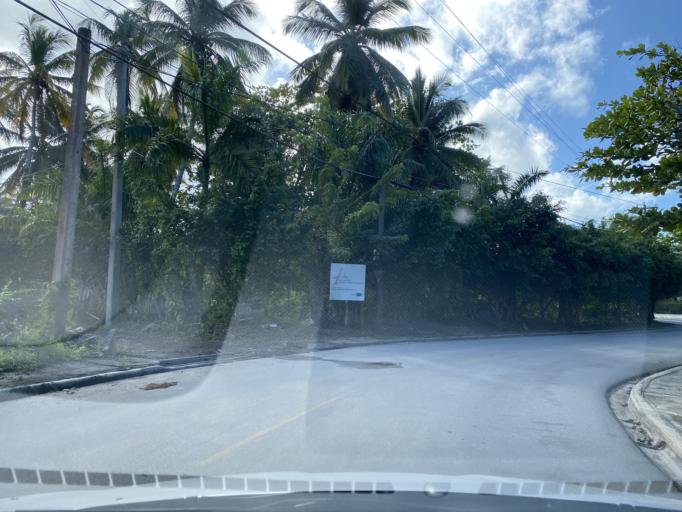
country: DO
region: Samana
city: Las Terrenas
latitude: 19.3110
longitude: -69.5682
